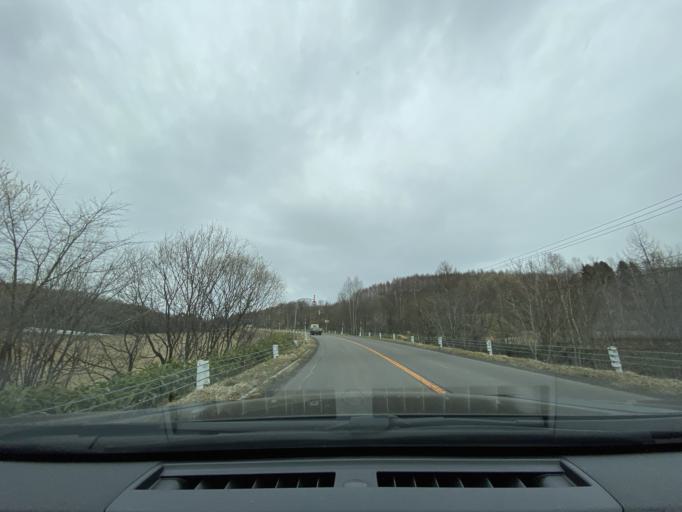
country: JP
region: Hokkaido
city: Nayoro
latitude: 44.0866
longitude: 142.4547
